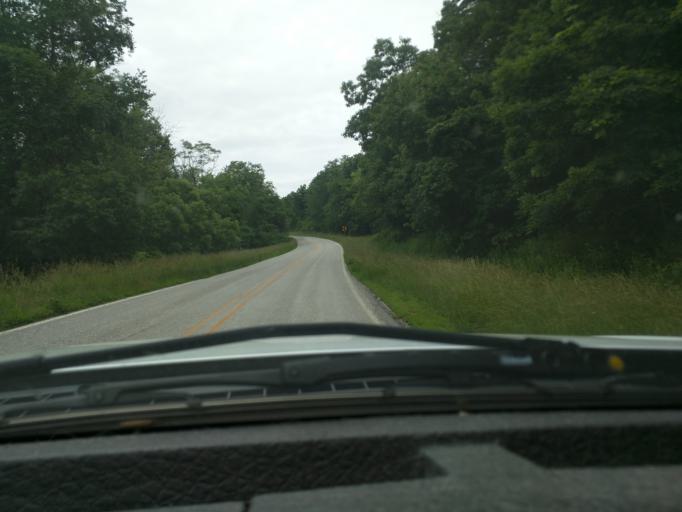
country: US
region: Arkansas
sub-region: Madison County
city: Huntsville
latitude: 35.8448
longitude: -93.5653
